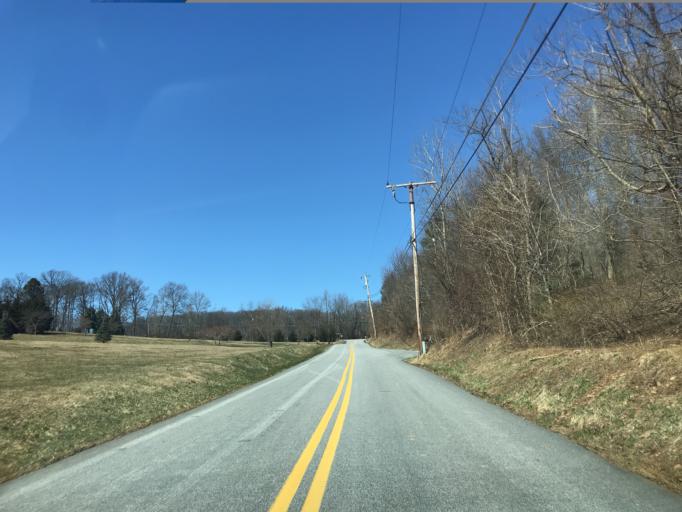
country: US
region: Pennsylvania
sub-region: York County
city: New Freedom
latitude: 39.6791
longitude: -76.6828
